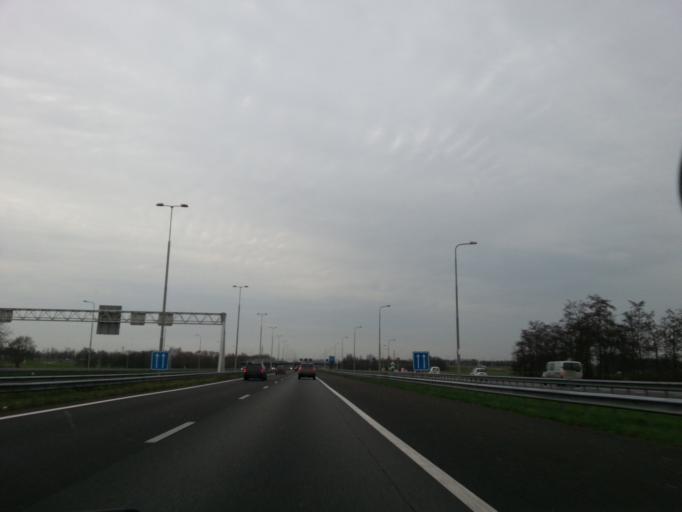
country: NL
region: Gelderland
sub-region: Gemeente Apeldoorn
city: Apeldoorn
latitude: 52.1822
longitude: 6.0262
